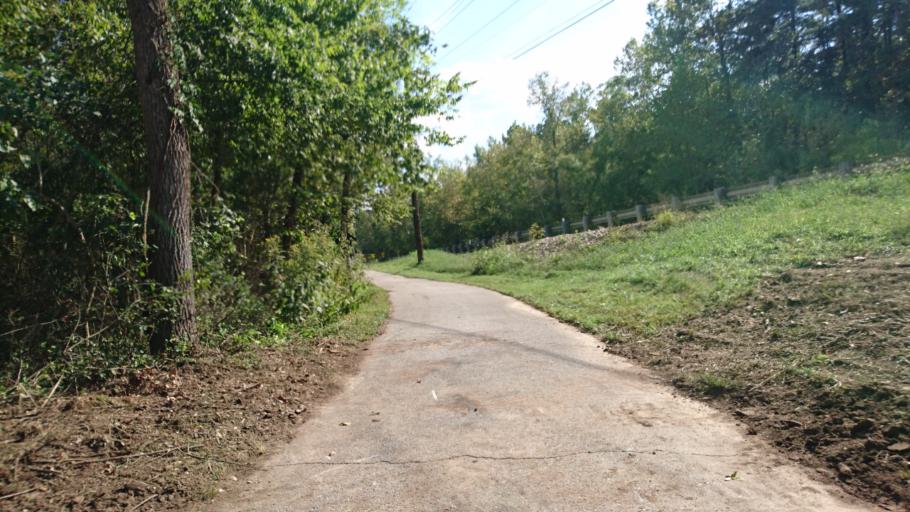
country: US
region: Missouri
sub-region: Saint Louis County
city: Wildwood
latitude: 38.5551
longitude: -90.6416
